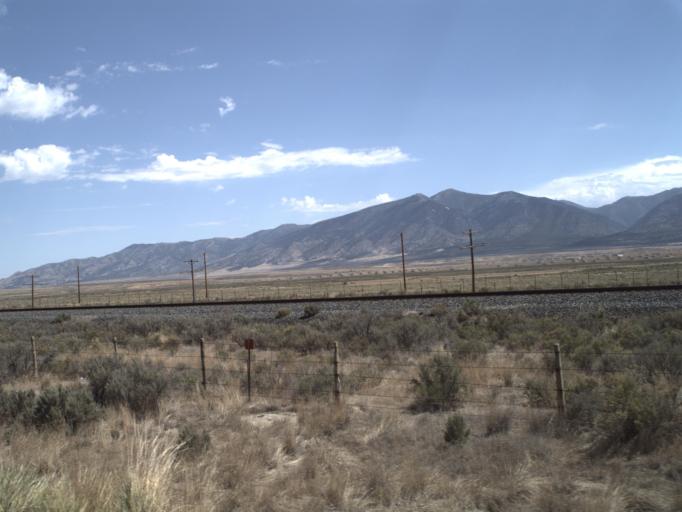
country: US
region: Utah
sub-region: Tooele County
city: Tooele
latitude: 40.2875
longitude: -112.4000
